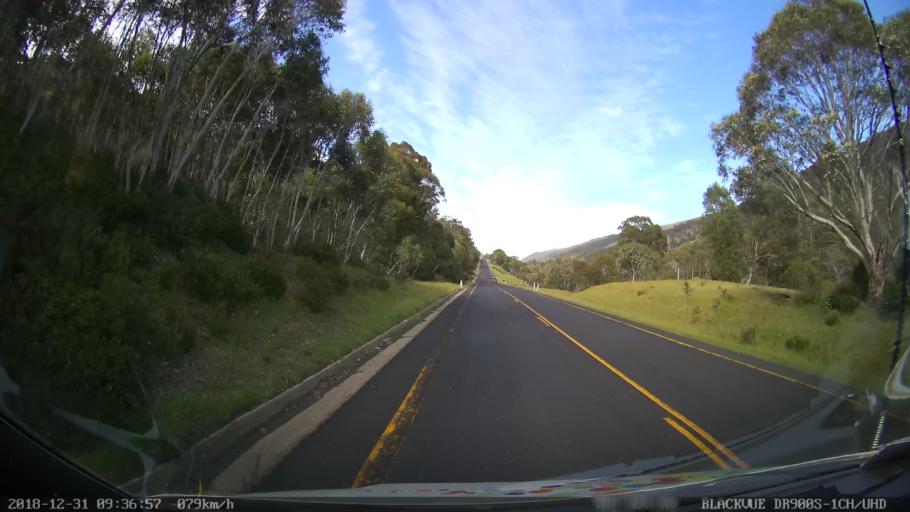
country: AU
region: New South Wales
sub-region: Snowy River
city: Jindabyne
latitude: -36.4628
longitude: 148.3813
